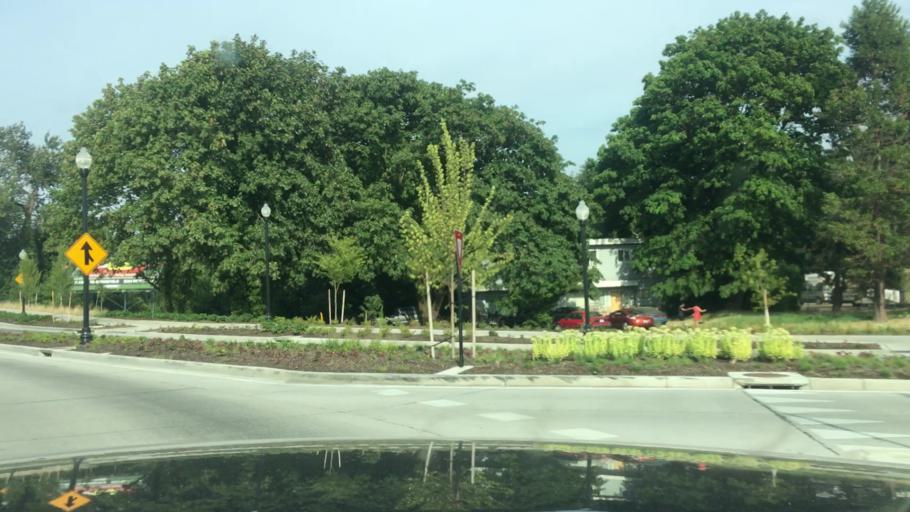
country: US
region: Oregon
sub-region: Lane County
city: Springfield
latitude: 44.0441
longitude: -123.0303
